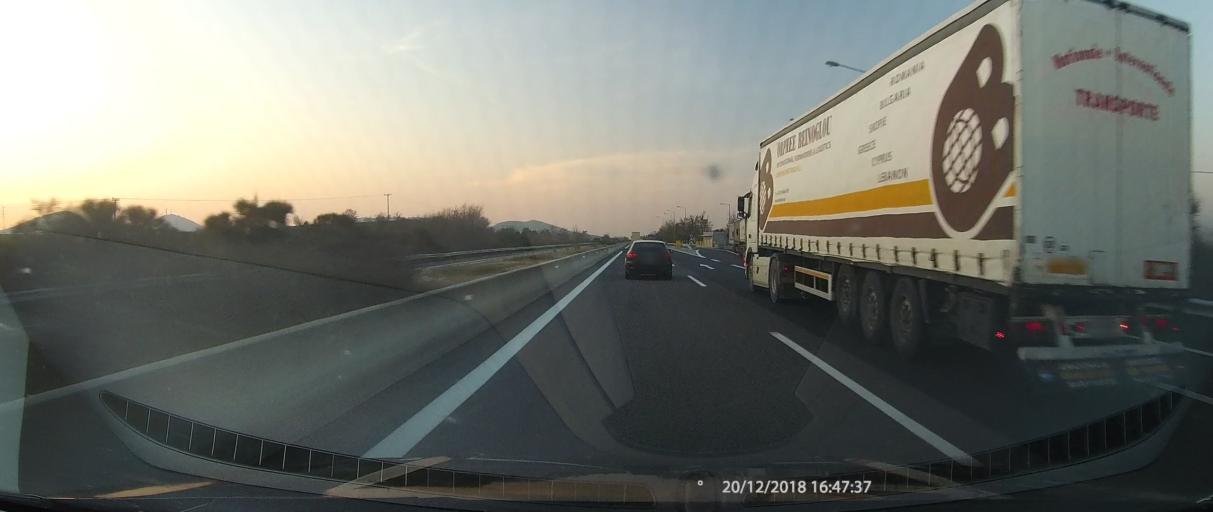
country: GR
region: Thessaly
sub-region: Nomos Magnisias
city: Stefanoviki
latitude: 39.4765
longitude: 22.6535
